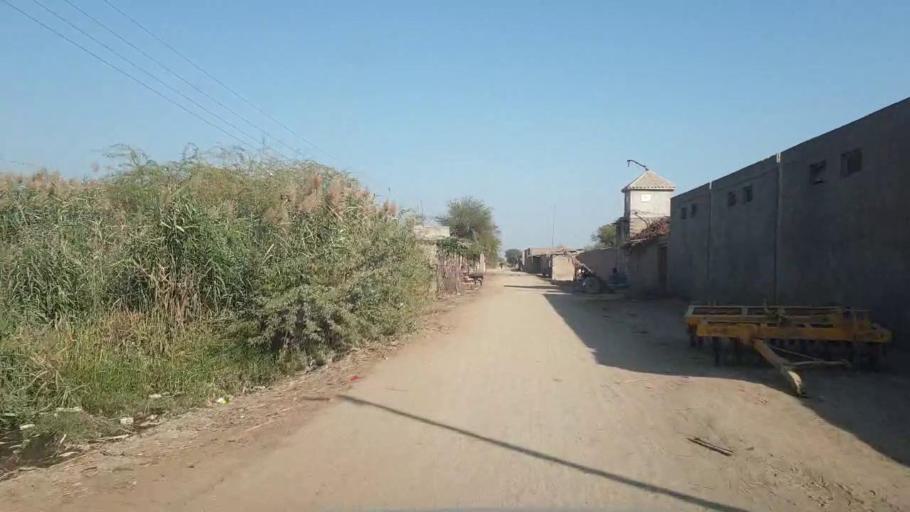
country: PK
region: Sindh
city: Chambar
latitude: 25.2882
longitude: 68.8633
